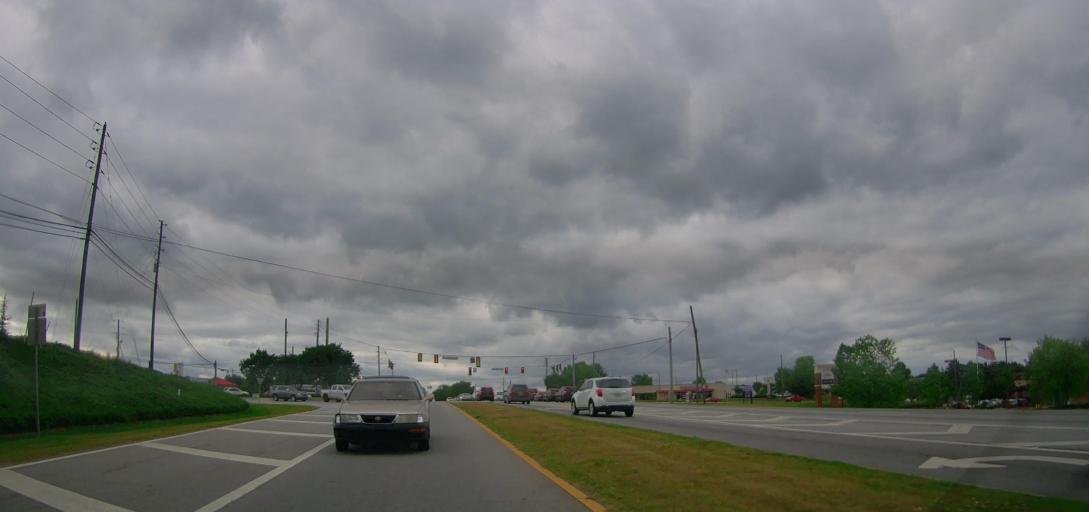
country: US
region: Georgia
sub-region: Walton County
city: Monroe
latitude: 33.7943
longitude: -83.7419
